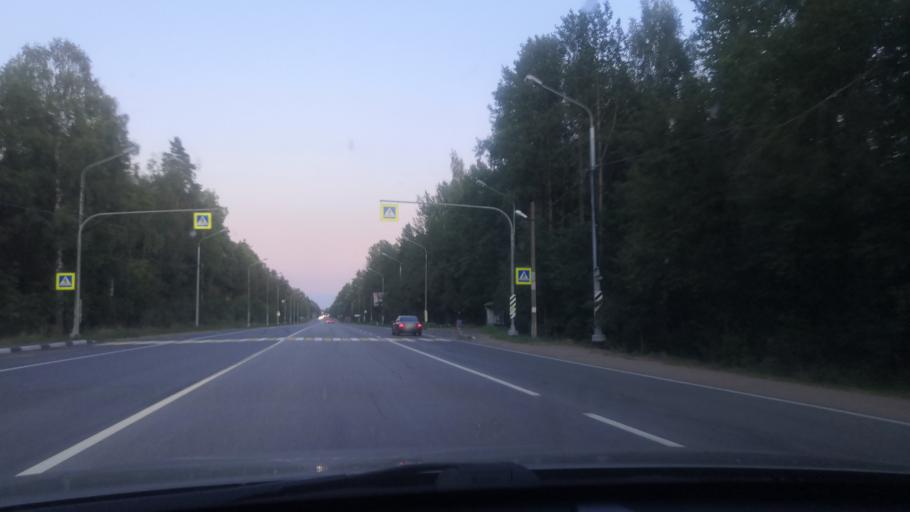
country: RU
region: St.-Petersburg
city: Pesochnyy
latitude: 60.1892
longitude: 30.0979
